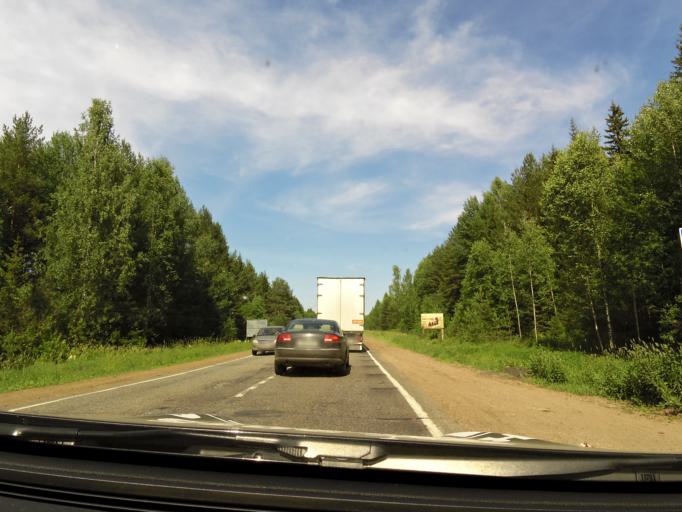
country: RU
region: Kirov
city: Belaya Kholunitsa
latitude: 58.8115
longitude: 50.5792
